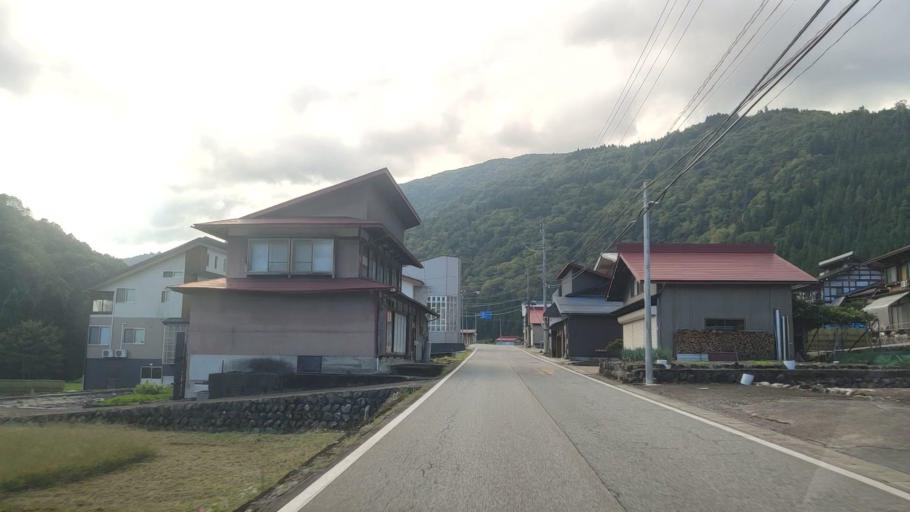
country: JP
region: Gifu
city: Takayama
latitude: 36.3056
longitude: 137.0942
